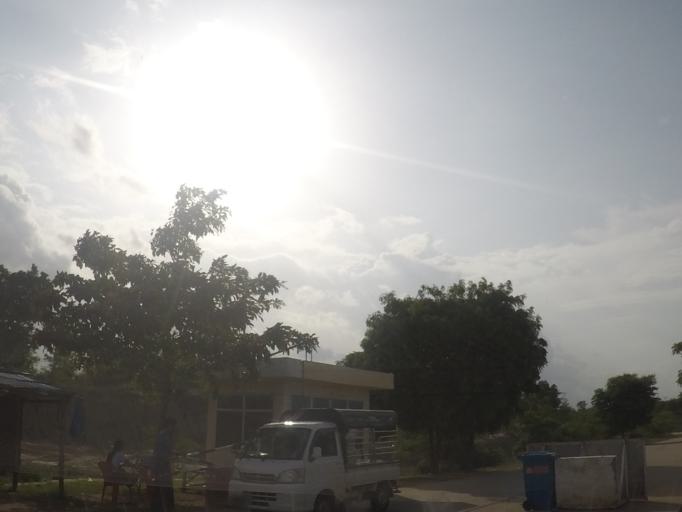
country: MM
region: Mandalay
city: Yamethin
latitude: 20.4956
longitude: 95.8247
